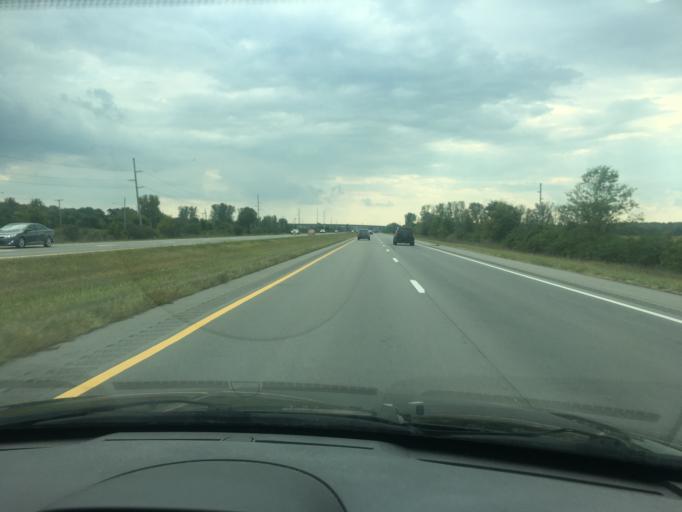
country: US
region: Ohio
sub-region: Clark County
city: Springfield
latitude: 39.9629
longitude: -83.8227
